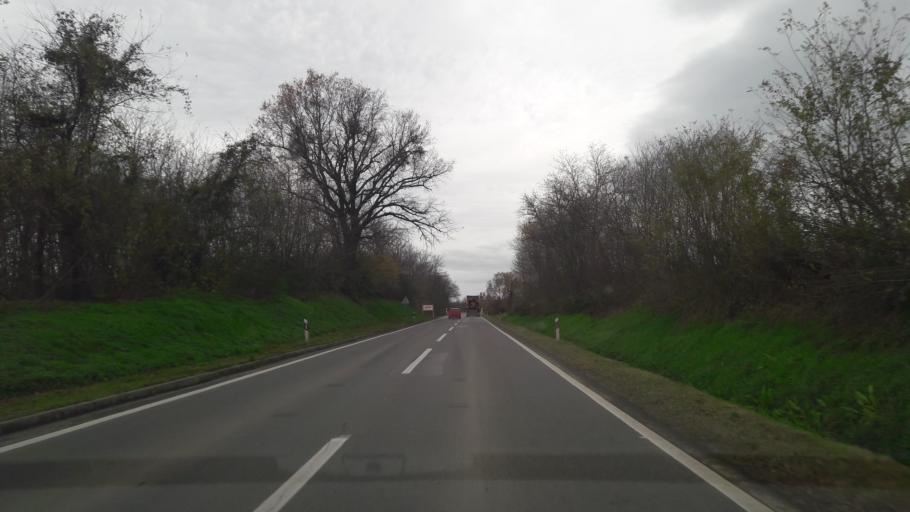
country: HR
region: Virovitick-Podravska
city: Orahovica
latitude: 45.5384
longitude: 17.9291
